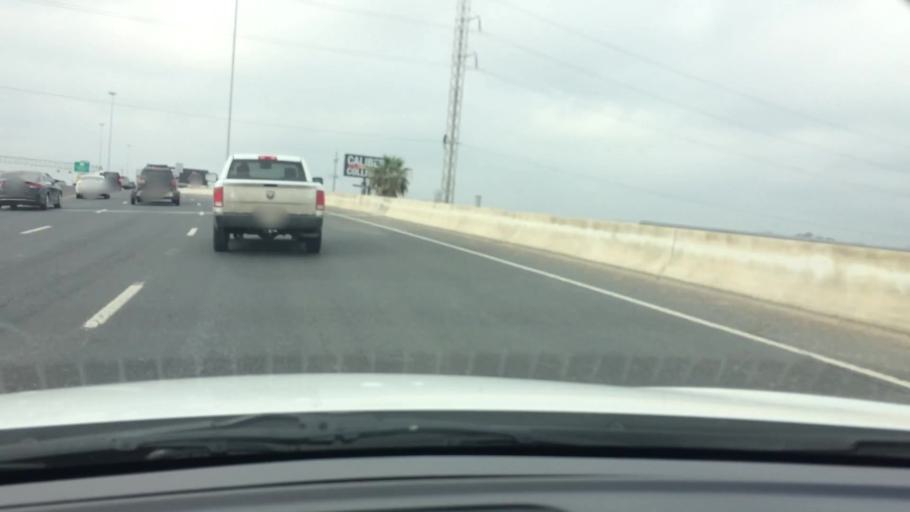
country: US
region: Texas
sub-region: Bexar County
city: San Antonio
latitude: 29.4399
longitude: -98.5064
